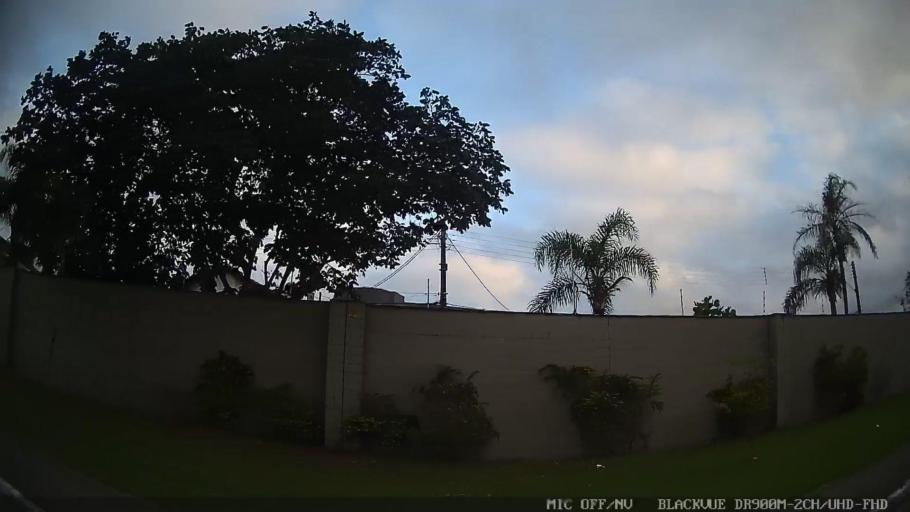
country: BR
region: Sao Paulo
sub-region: Peruibe
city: Peruibe
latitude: -24.3033
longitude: -46.9893
